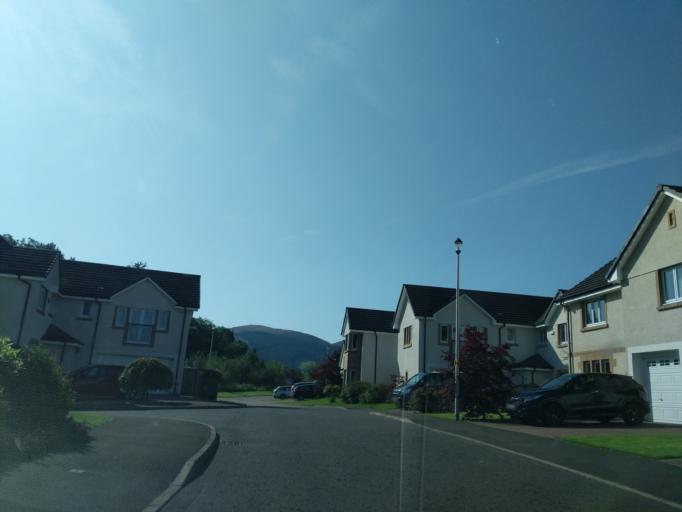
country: GB
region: Scotland
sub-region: The Scottish Borders
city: Peebles
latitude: 55.6414
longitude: -3.1860
